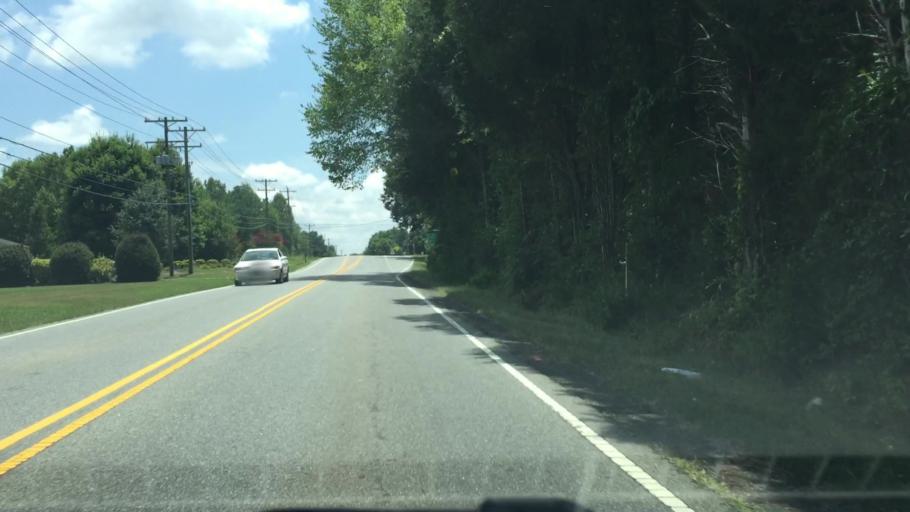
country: US
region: North Carolina
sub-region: Rowan County
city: Enochville
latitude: 35.4351
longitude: -80.7255
